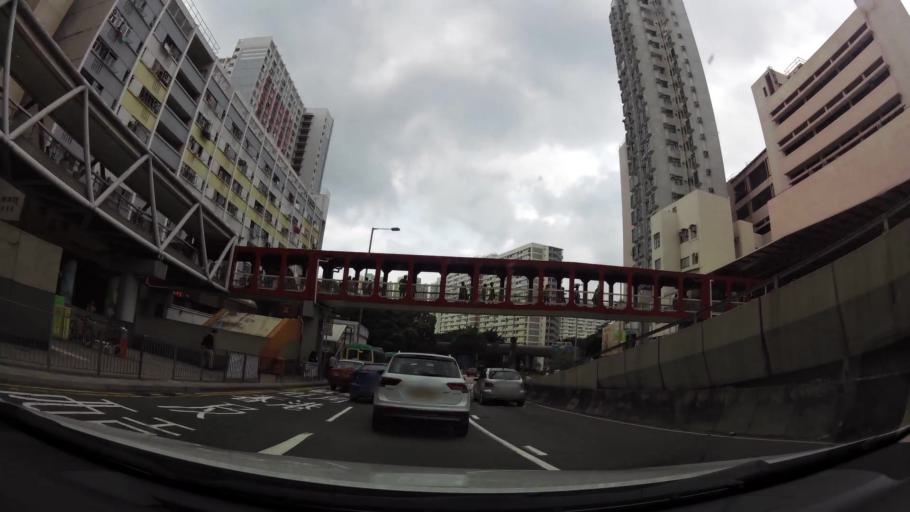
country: HK
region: Wong Tai Sin
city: Wong Tai Sin
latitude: 22.3342
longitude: 114.2095
